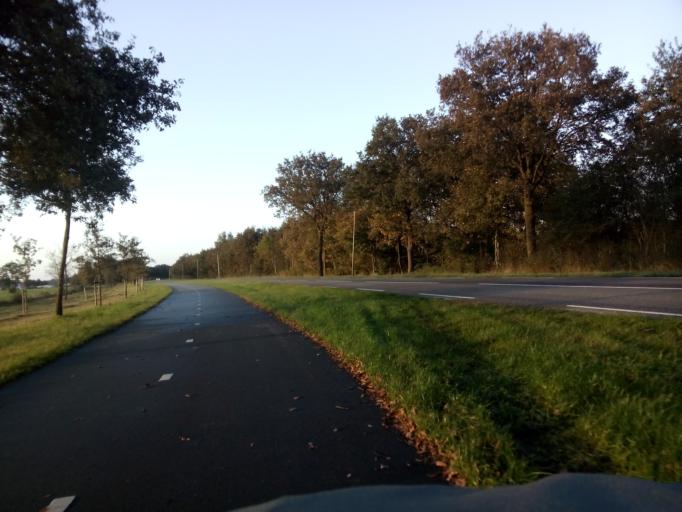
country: NL
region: Overijssel
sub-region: Gemeente Staphorst
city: Staphorst
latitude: 52.6675
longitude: 6.1957
